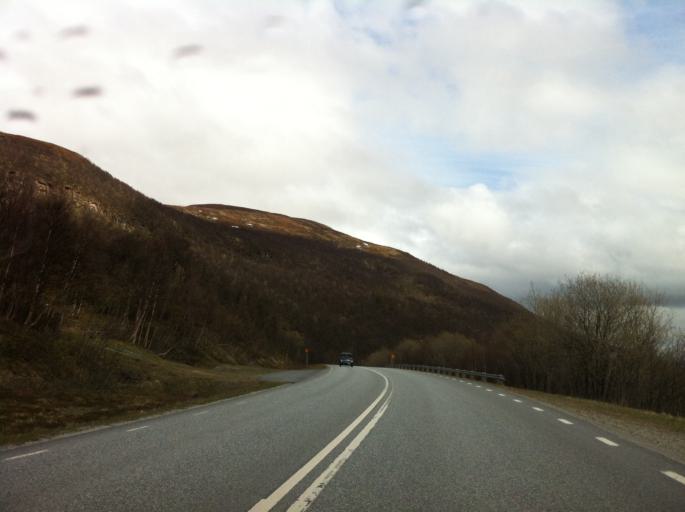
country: NO
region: Sor-Trondelag
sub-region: Tydal
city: Aas
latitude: 62.5715
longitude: 12.2330
